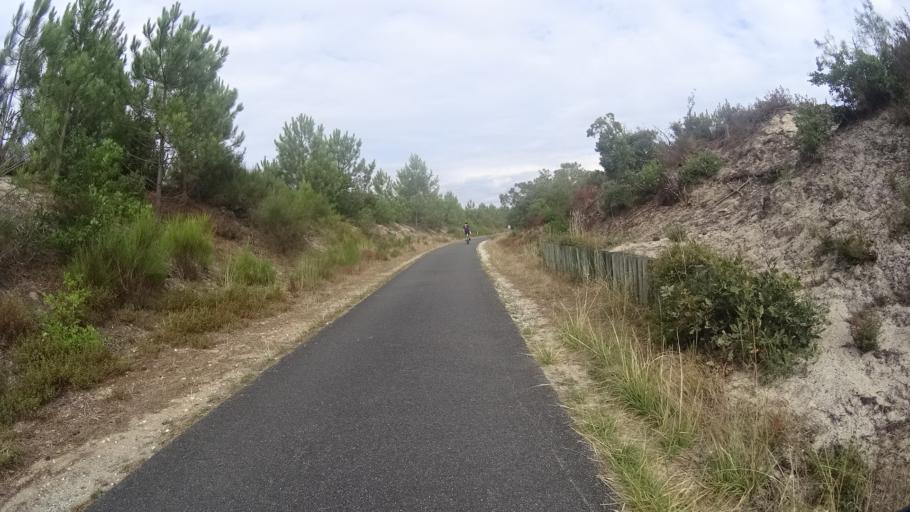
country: FR
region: Aquitaine
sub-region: Departement de la Gironde
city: Lacanau
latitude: 45.0068
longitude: -1.1607
